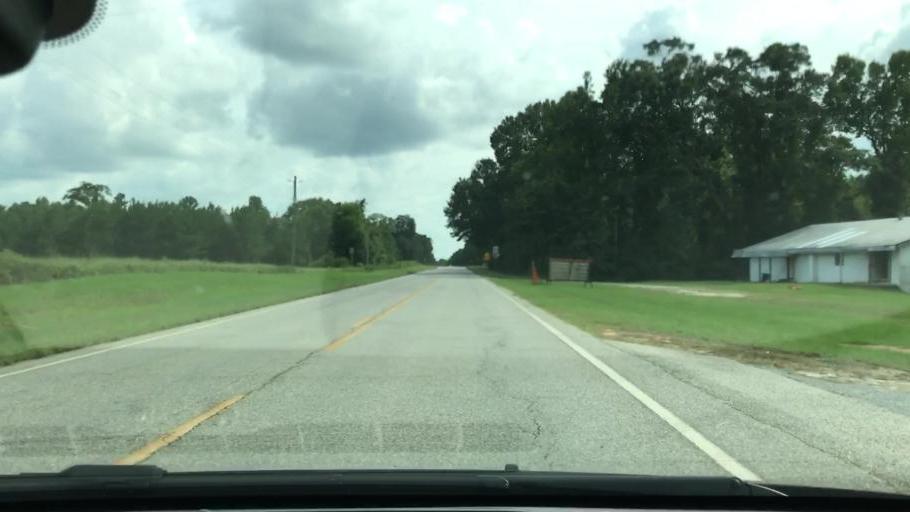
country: US
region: Georgia
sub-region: Clay County
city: Fort Gaines
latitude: 31.6659
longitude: -85.0472
